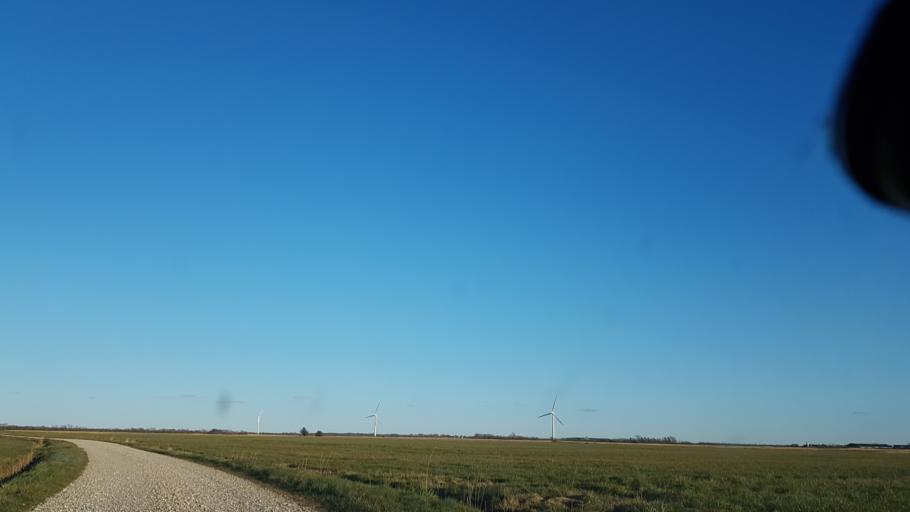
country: DK
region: South Denmark
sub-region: Esbjerg Kommune
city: Bramming
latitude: 55.4140
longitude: 8.6636
